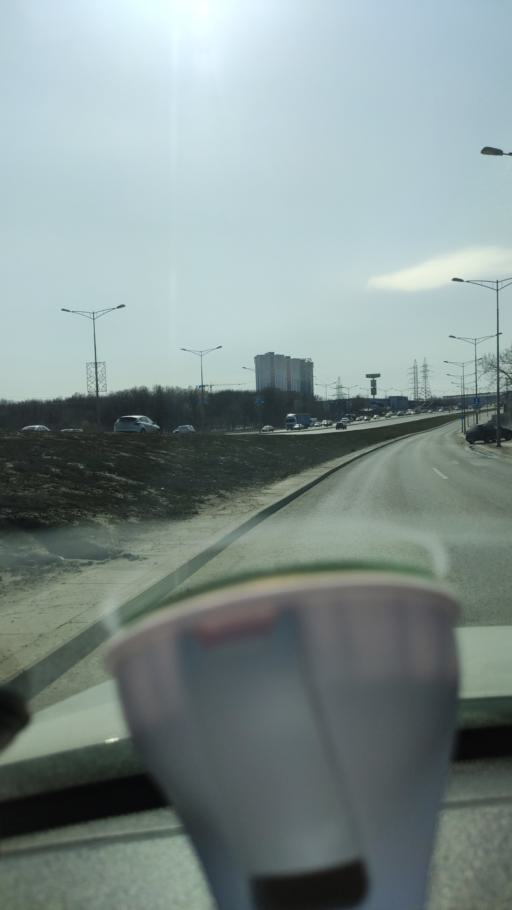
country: RU
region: Samara
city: Petra-Dubrava
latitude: 53.2845
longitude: 50.2816
